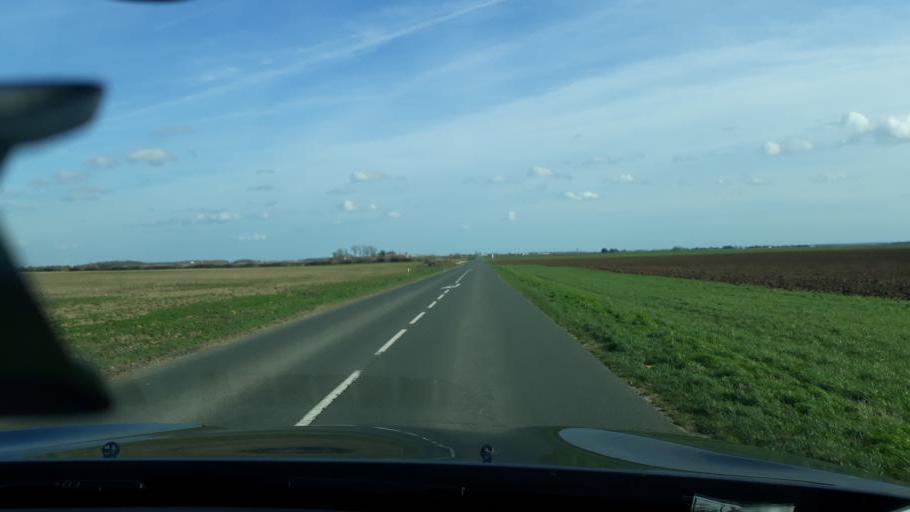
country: FR
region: Centre
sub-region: Departement du Loiret
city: Artenay
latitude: 48.0804
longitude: 1.9084
